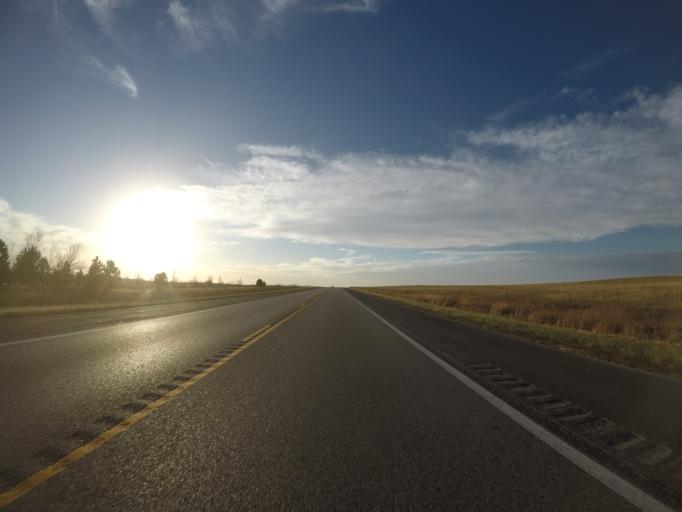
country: US
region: Kansas
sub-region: Chase County
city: Cottonwood Falls
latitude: 38.4055
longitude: -96.4361
